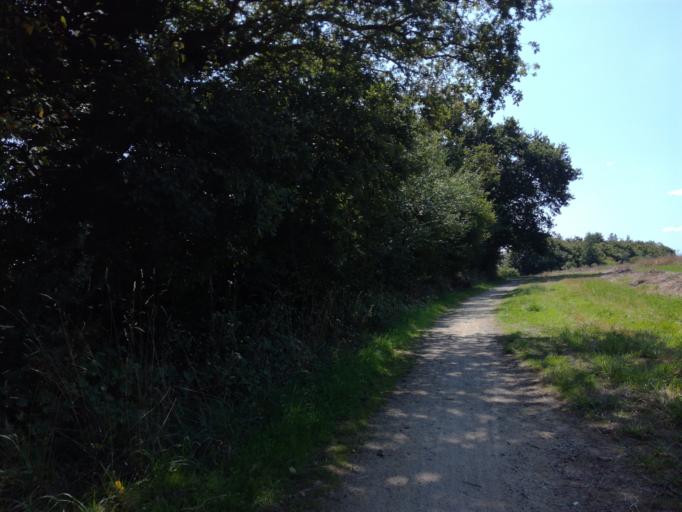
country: FR
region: Brittany
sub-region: Departement d'Ille-et-Vilaine
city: Cesson-Sevigne
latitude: 48.1343
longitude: -1.5900
